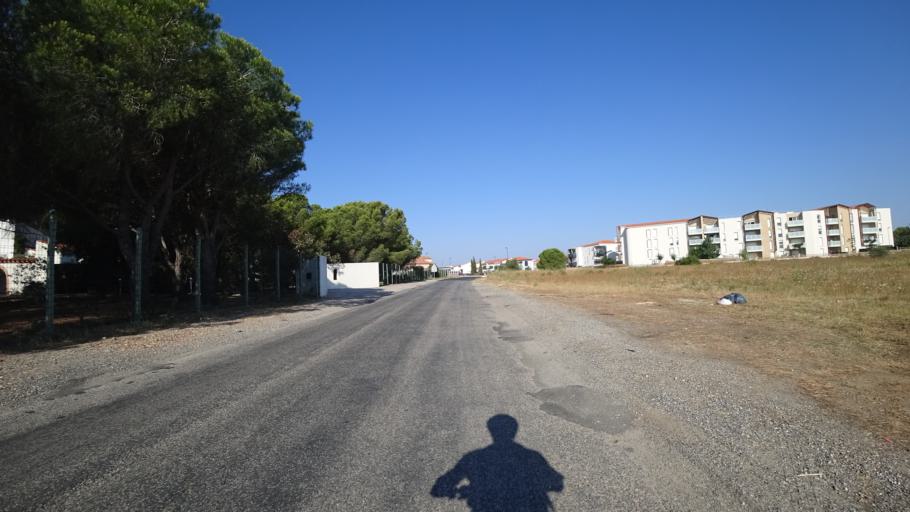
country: FR
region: Languedoc-Roussillon
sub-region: Departement des Pyrenees-Orientales
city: Cabestany
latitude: 42.6844
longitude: 2.9517
